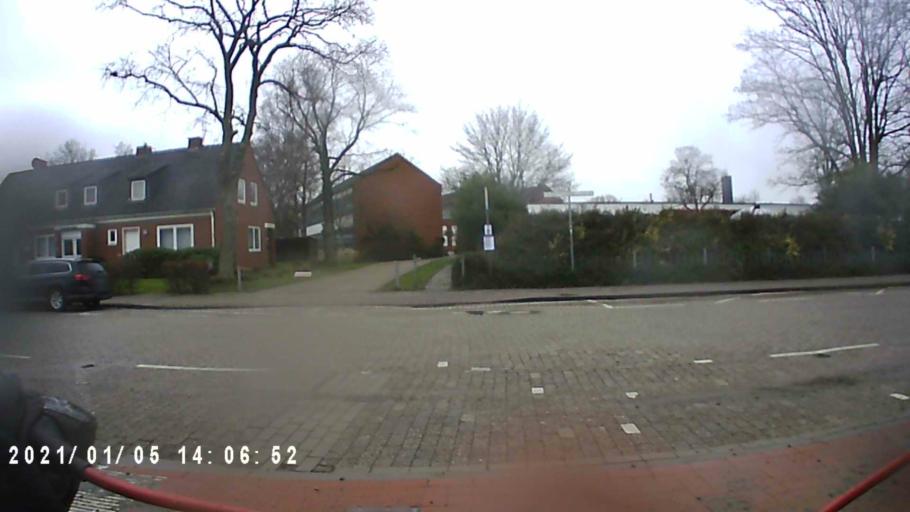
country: DE
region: Lower Saxony
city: Weener
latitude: 53.1642
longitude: 7.3431
